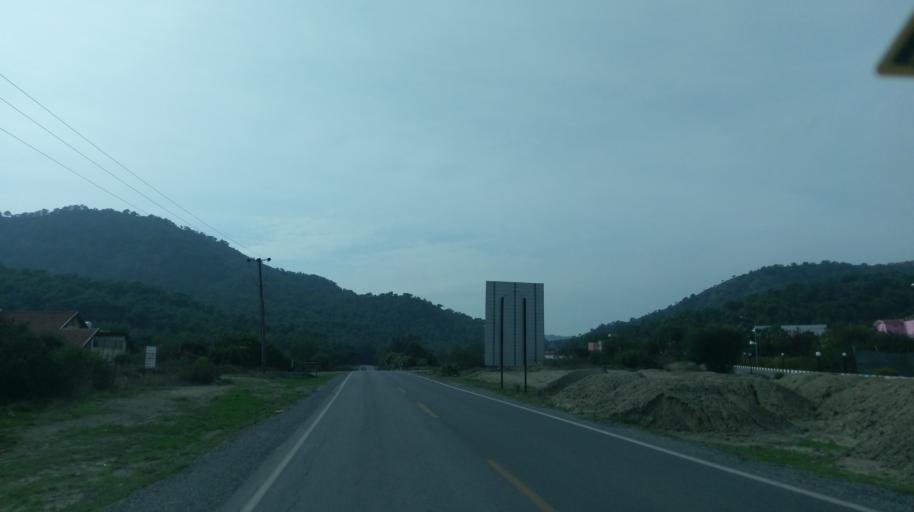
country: CY
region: Keryneia
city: Lapithos
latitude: 35.3480
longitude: 33.0824
